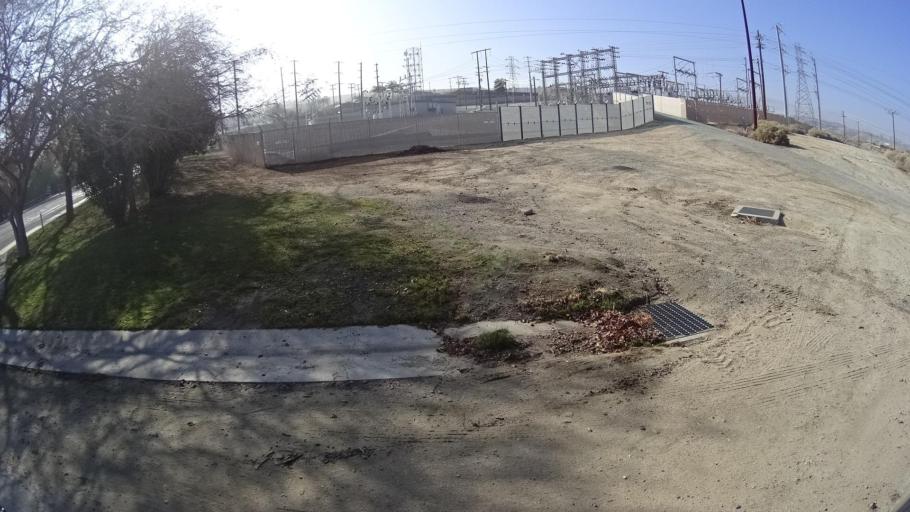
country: US
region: California
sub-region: Kern County
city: Taft Heights
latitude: 35.1370
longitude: -119.4811
